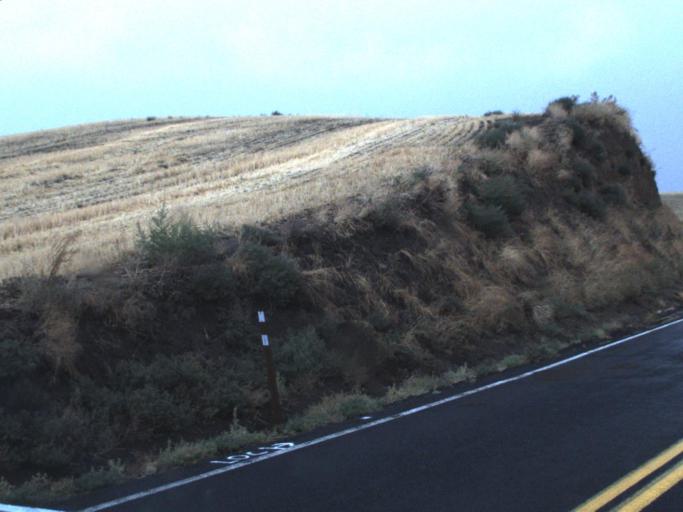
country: US
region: Washington
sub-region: Spokane County
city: Cheney
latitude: 47.1962
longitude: -117.8786
